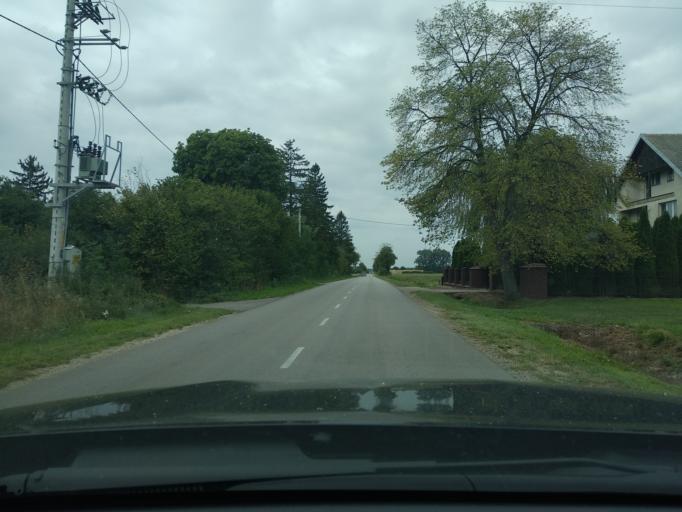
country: PL
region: Masovian Voivodeship
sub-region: Powiat pultuski
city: Obryte
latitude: 52.7153
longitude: 21.2194
